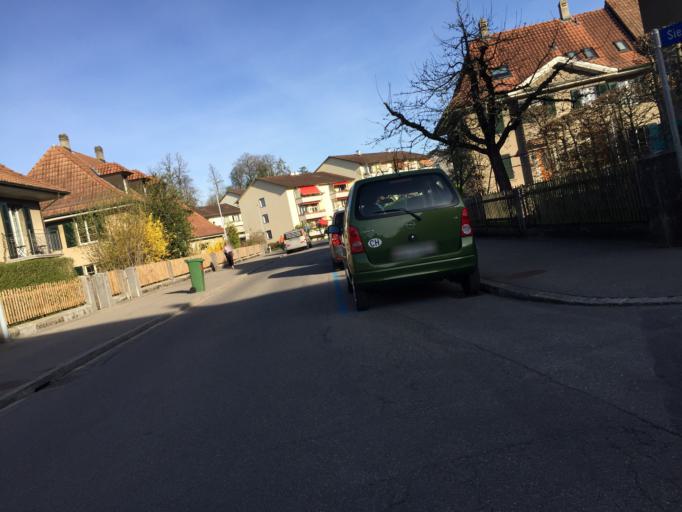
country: CH
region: Bern
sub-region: Bern-Mittelland District
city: Koniz
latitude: 46.9387
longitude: 7.4215
